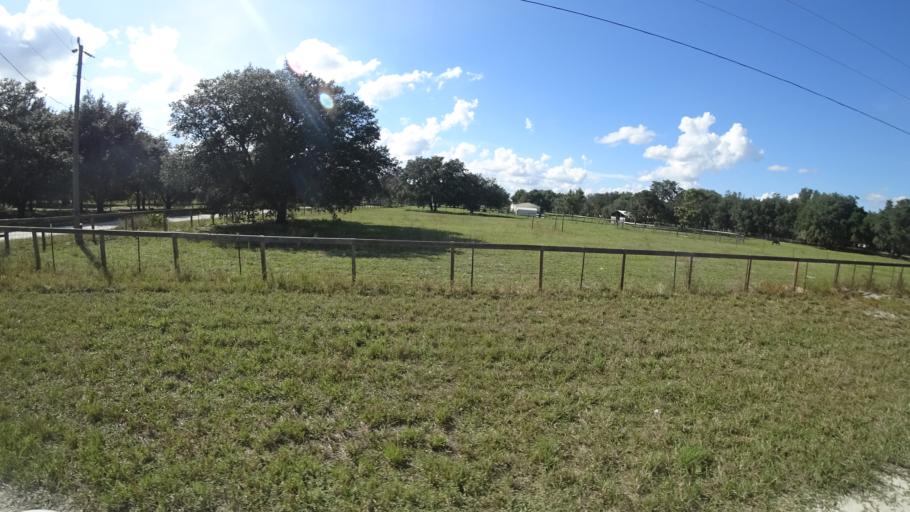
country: US
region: Florida
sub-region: Hardee County
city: Wauchula
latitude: 27.4824
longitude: -82.0554
